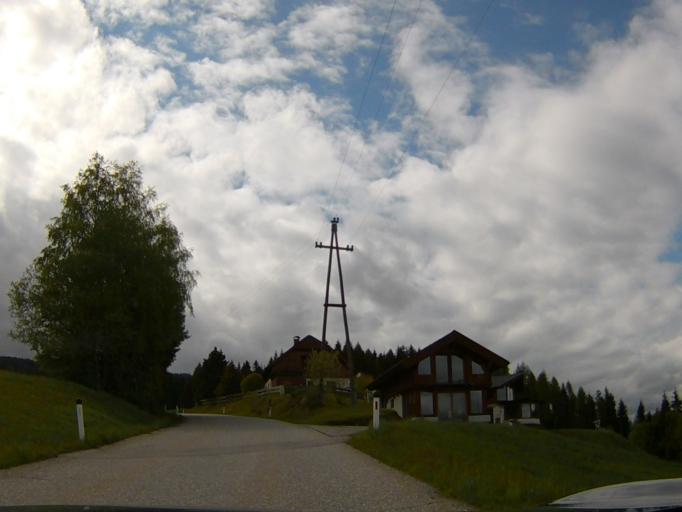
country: AT
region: Carinthia
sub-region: Politischer Bezirk Villach Land
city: Stockenboi
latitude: 46.7379
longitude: 13.5561
